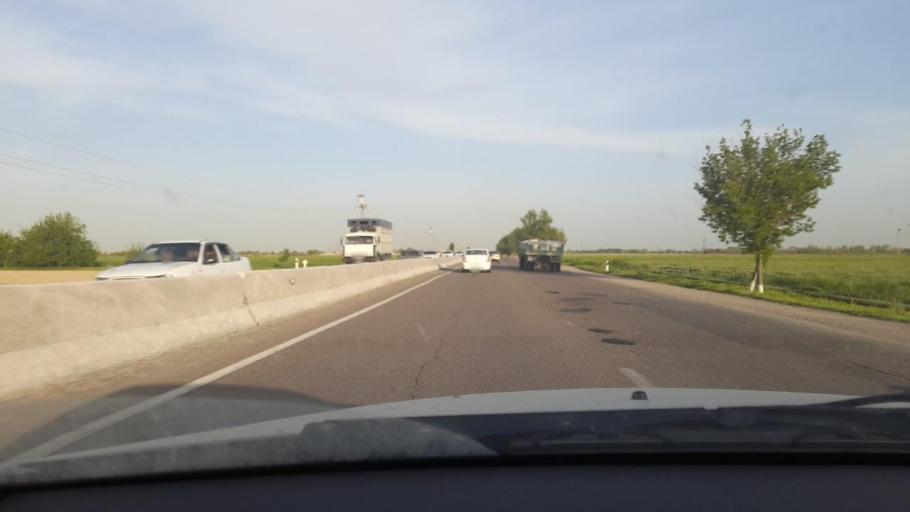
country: KZ
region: Ongtustik Qazaqstan
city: Myrzakent
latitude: 40.5584
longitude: 68.3871
